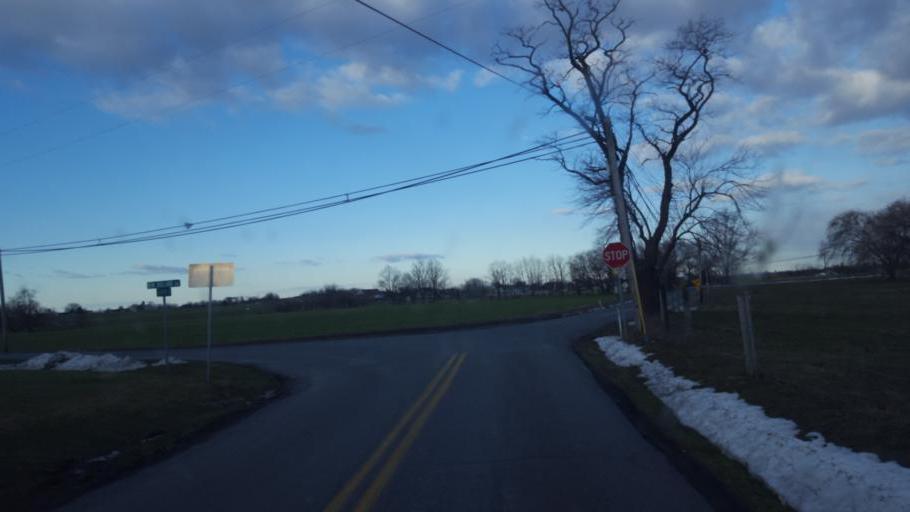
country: US
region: Pennsylvania
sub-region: Lancaster County
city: New Holland
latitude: 40.0679
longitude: -76.0677
